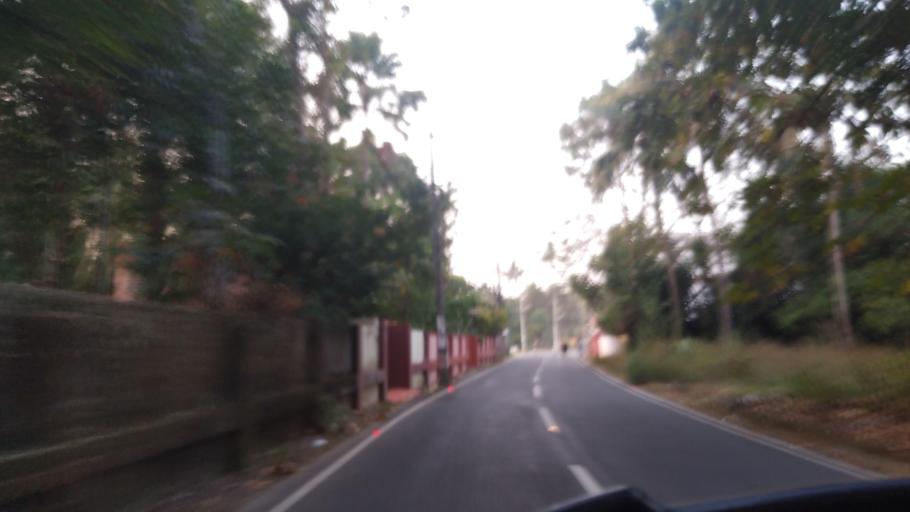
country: IN
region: Kerala
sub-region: Ernakulam
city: Elur
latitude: 10.1087
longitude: 76.2451
